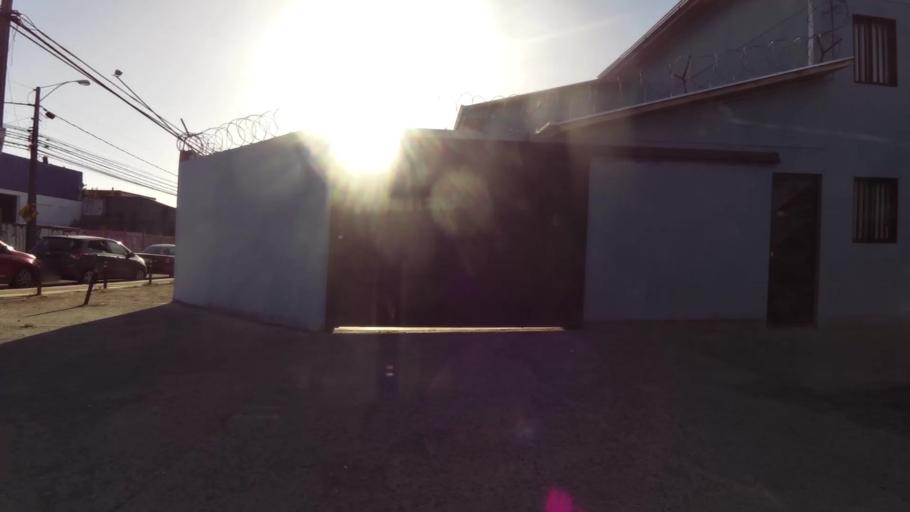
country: CL
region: Maule
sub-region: Provincia de Talca
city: Talca
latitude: -35.4299
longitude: -71.6557
